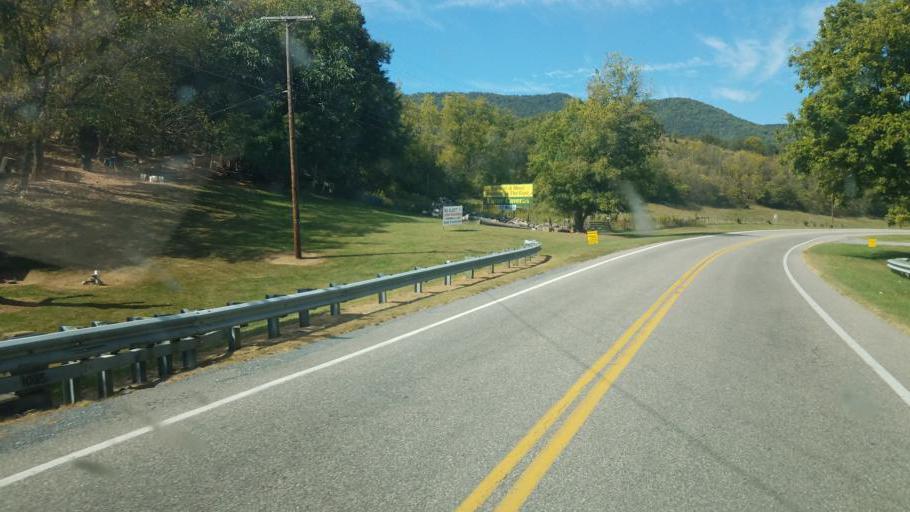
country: US
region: Virginia
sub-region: Page County
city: Stanley
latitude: 38.5789
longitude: -78.5963
